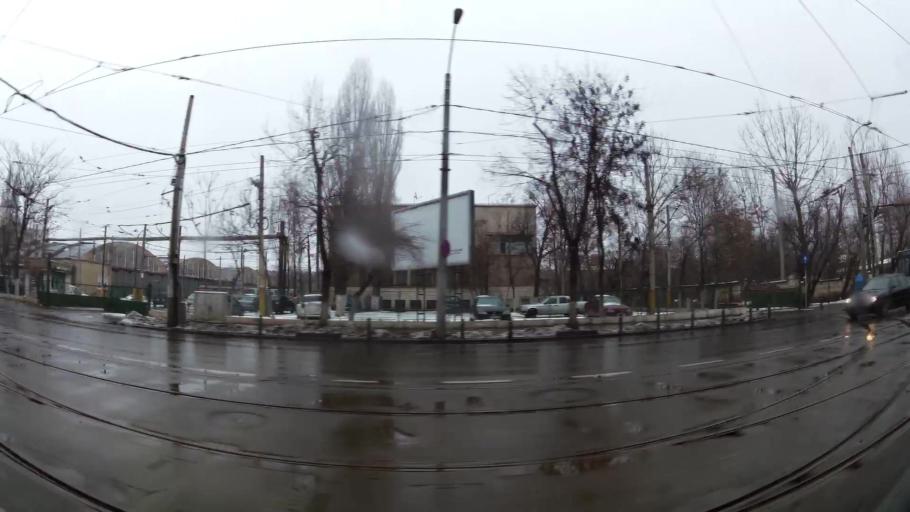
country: RO
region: Ilfov
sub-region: Comuna Chiajna
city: Rosu
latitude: 44.4781
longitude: 26.0445
